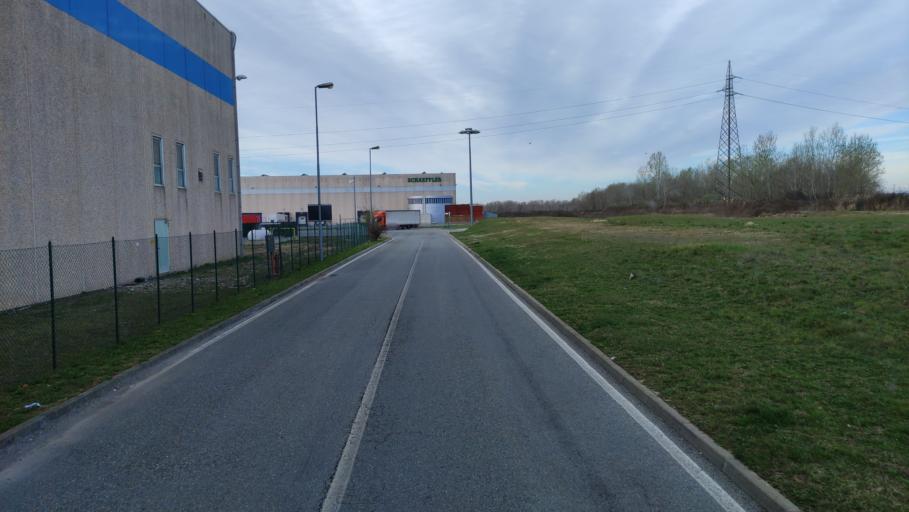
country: IT
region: Piedmont
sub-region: Provincia di Vercelli
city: Carisio
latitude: 45.4320
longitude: 8.2112
